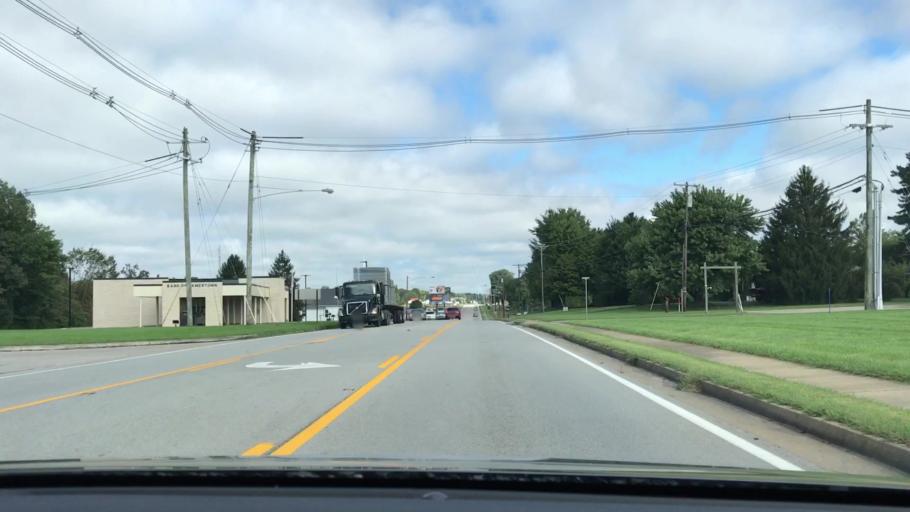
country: US
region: Kentucky
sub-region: Russell County
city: Jamestown
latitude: 37.0134
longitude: -85.0756
